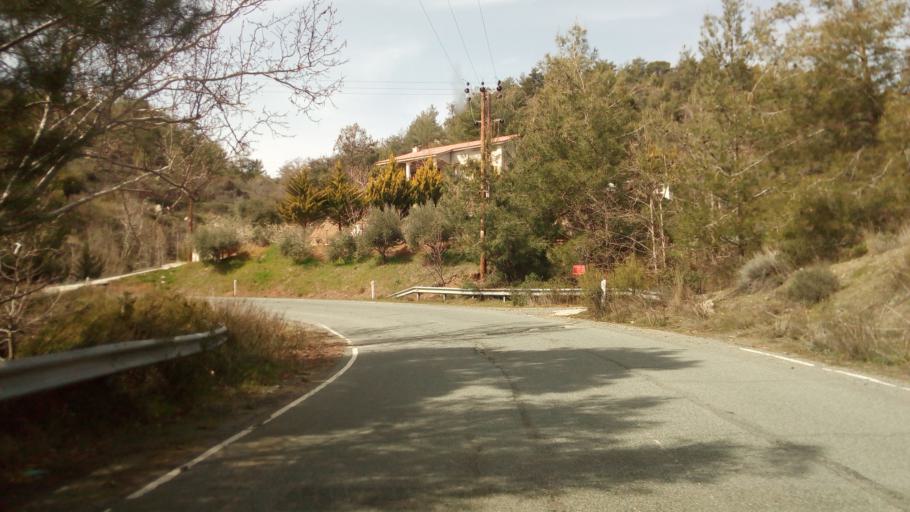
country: CY
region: Limassol
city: Pelendri
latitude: 34.8944
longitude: 32.9803
